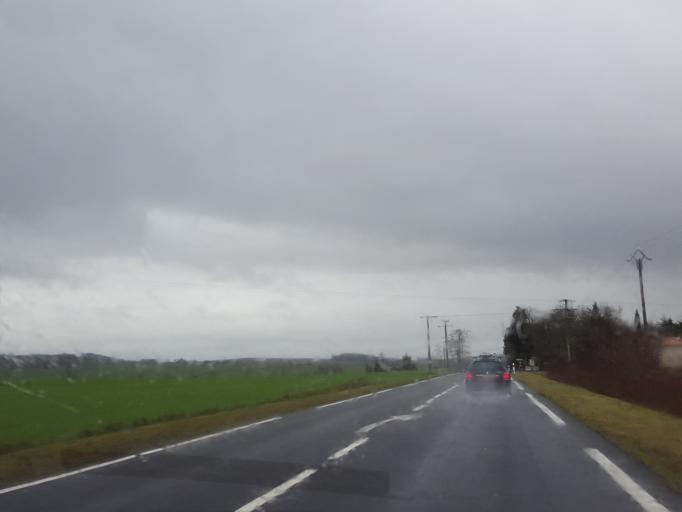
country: FR
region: Languedoc-Roussillon
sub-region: Departement de l'Aude
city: Bram
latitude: 43.1781
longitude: 2.0201
